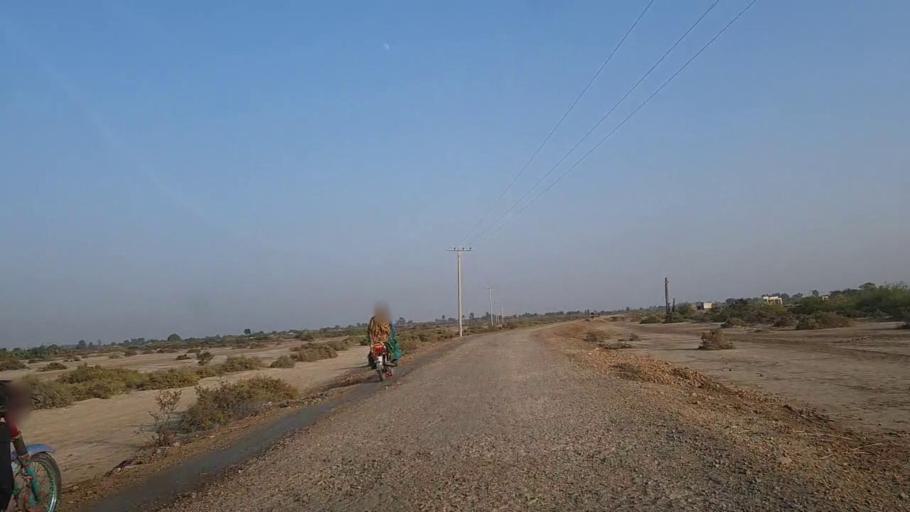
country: PK
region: Sindh
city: Keti Bandar
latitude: 24.2791
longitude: 67.6418
